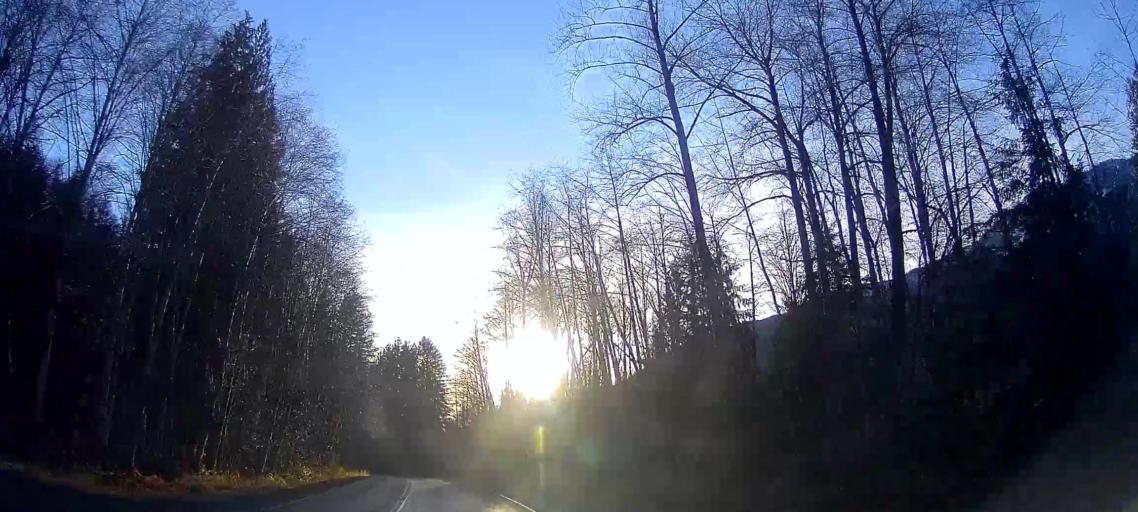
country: US
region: Washington
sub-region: Snohomish County
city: Darrington
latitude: 48.6011
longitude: -121.7652
